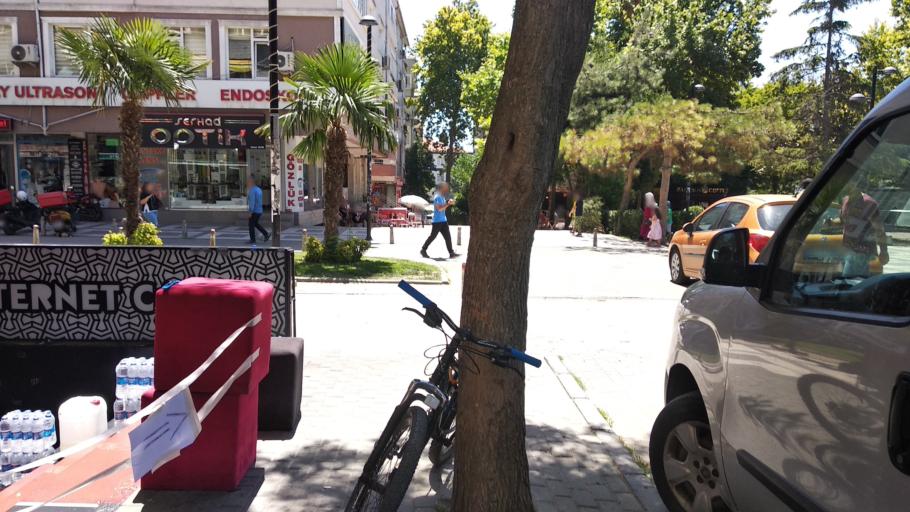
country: TR
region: Istanbul
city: Yakuplu
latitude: 40.9790
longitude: 28.7221
